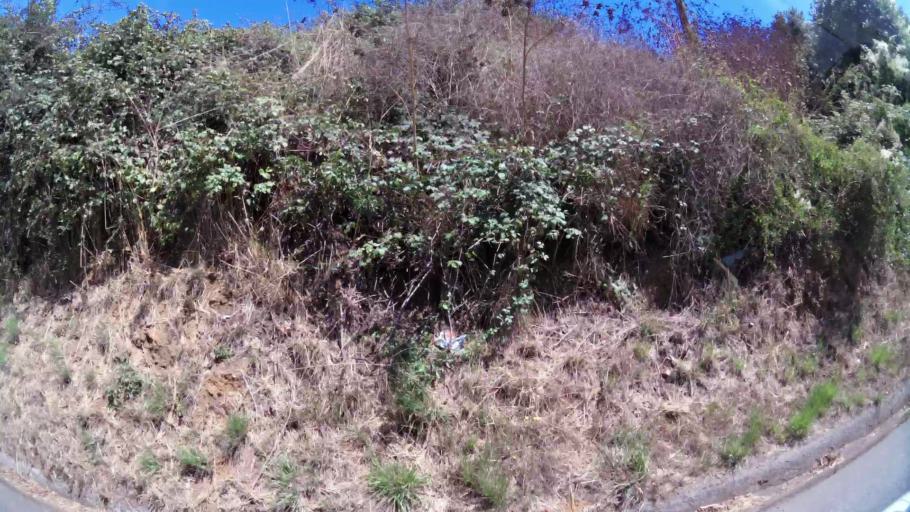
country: CL
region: Biobio
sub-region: Provincia de Concepcion
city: Talcahuano
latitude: -36.7137
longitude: -73.1263
